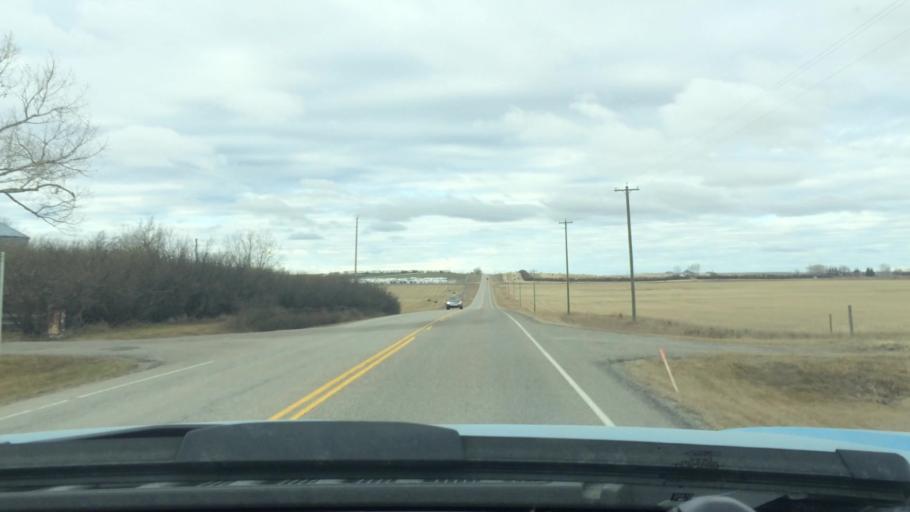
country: CA
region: Alberta
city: Airdrie
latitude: 51.2126
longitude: -114.0362
